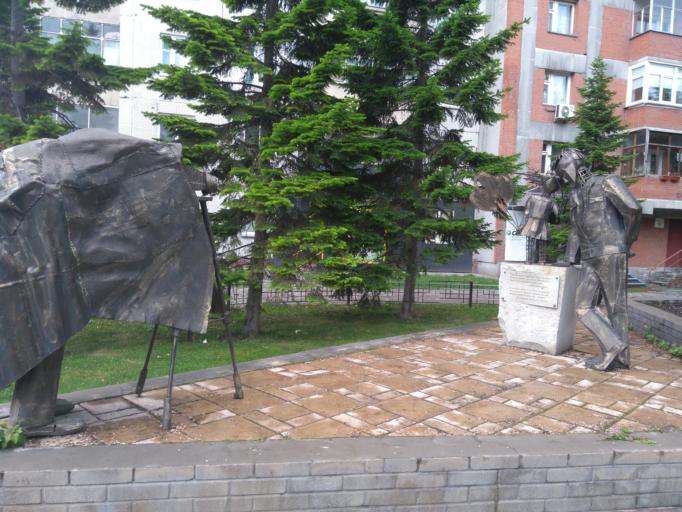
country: RU
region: Novosibirsk
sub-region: Novosibirskiy Rayon
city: Novosibirsk
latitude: 55.0494
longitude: 82.8861
